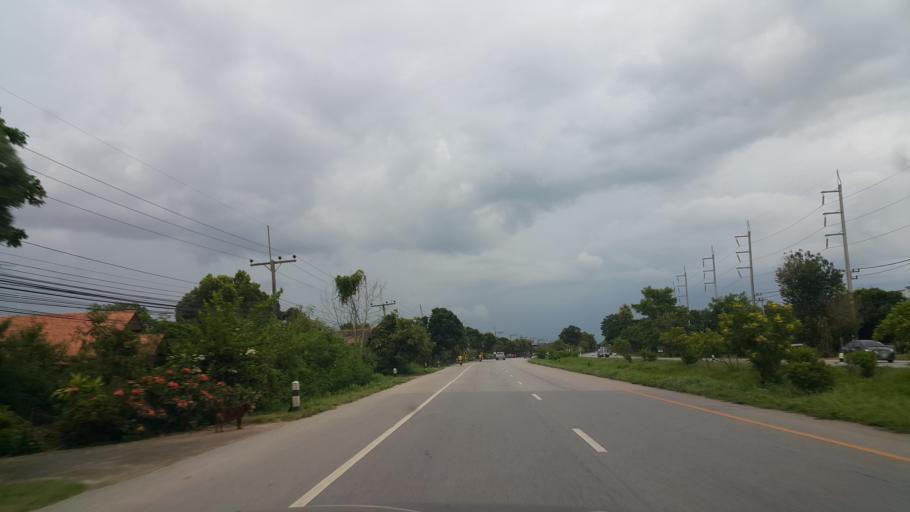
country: TH
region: Phayao
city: Phayao
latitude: 19.1159
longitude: 99.9056
